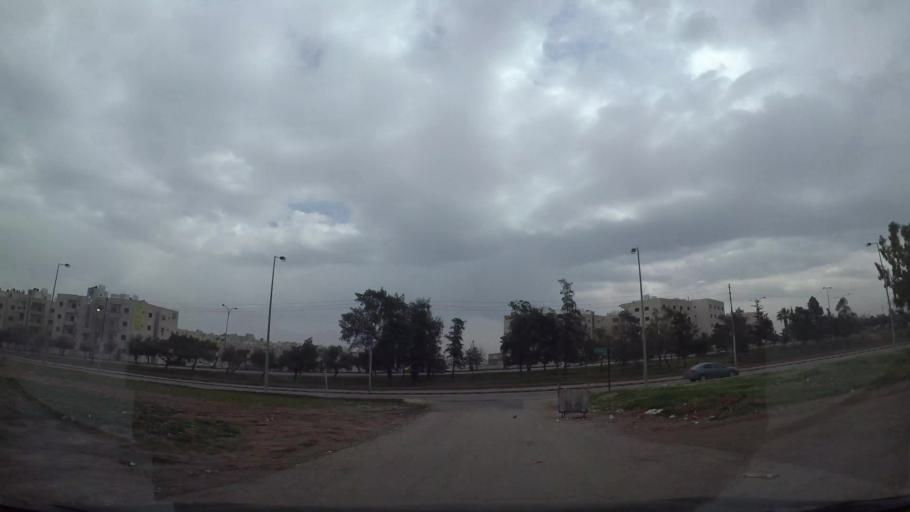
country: JO
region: Amman
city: Amman
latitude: 31.9754
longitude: 35.9334
